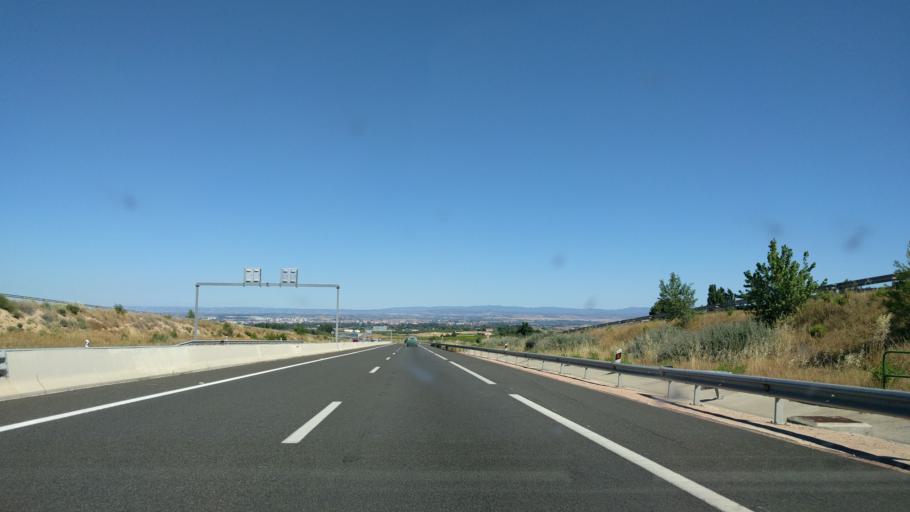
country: ES
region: Catalonia
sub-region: Provincia de Lleida
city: Alpicat
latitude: 41.6605
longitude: 0.5294
